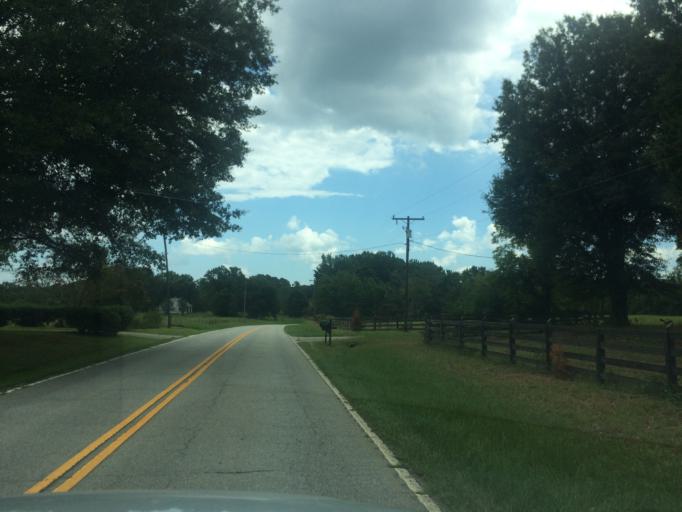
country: US
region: South Carolina
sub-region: Spartanburg County
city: Inman
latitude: 35.1844
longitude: -82.0423
